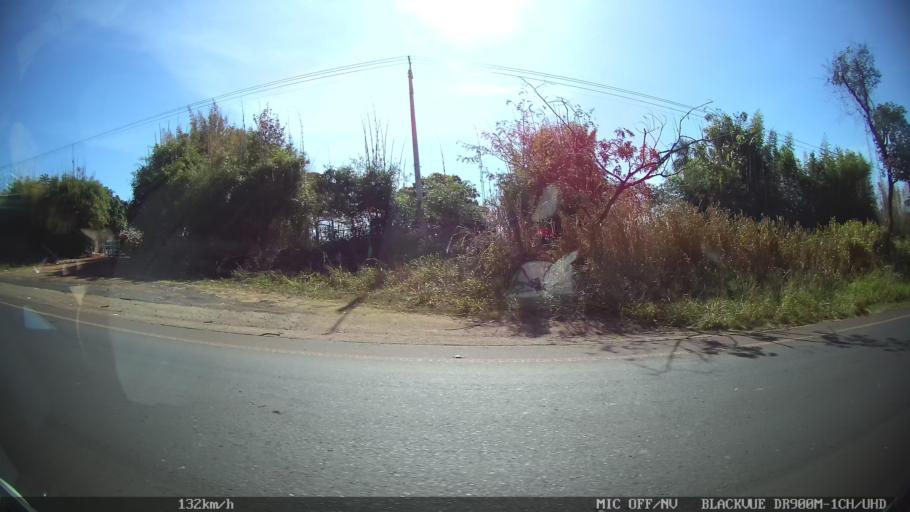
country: BR
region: Sao Paulo
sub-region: Barretos
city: Barretos
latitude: -20.5487
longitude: -48.6301
